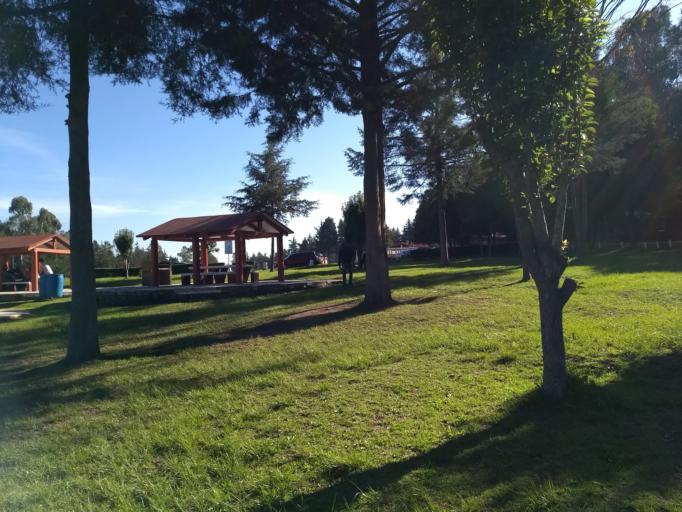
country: MX
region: Mexico
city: San Marcos Yachihuacaltepec
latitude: 19.3109
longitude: -99.6864
